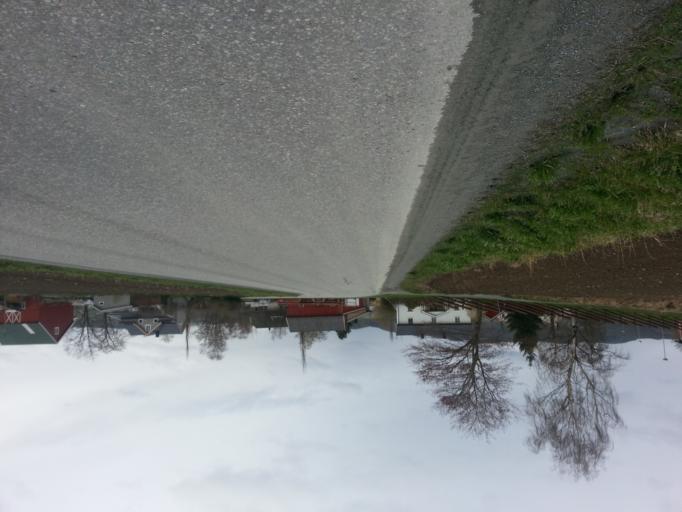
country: NO
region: Nord-Trondelag
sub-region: Levanger
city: Skogn
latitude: 63.6967
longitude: 11.1987
